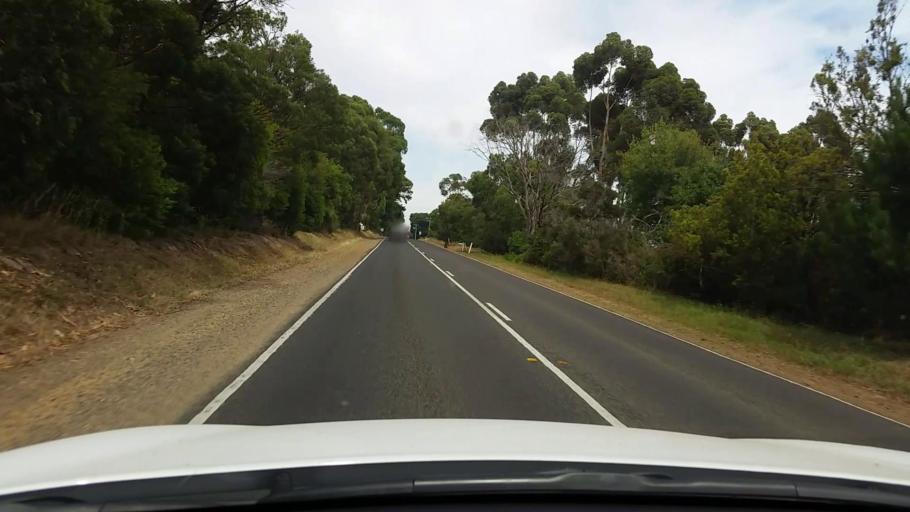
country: AU
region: Victoria
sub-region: Mornington Peninsula
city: Merricks
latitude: -38.3862
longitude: 145.0991
